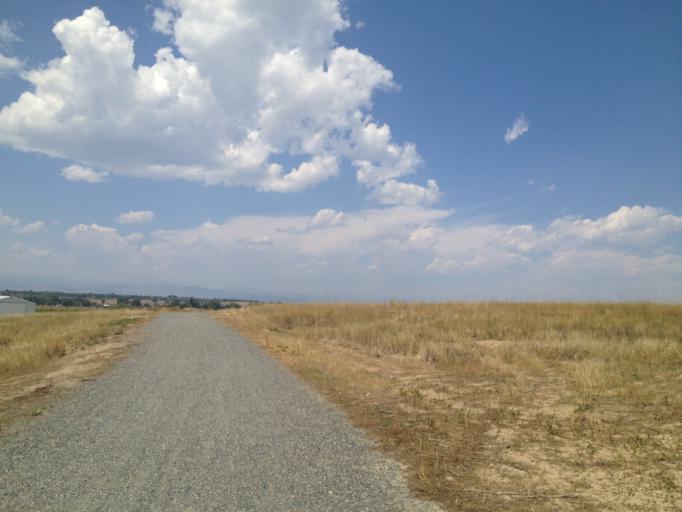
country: US
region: Colorado
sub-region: Boulder County
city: Lafayette
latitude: 39.9953
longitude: -105.0558
